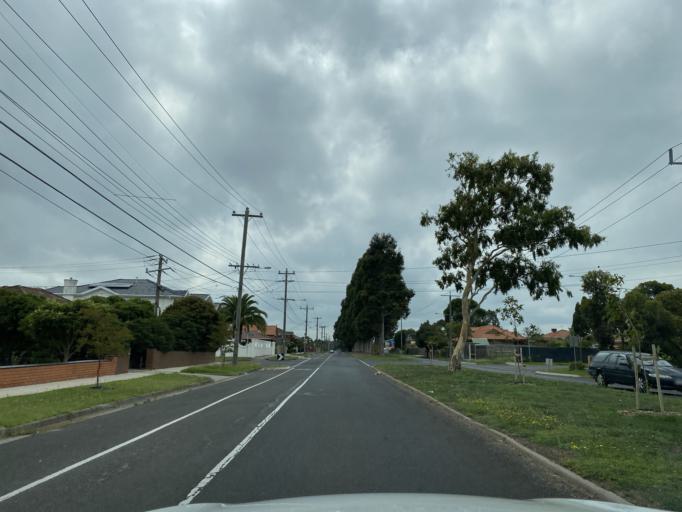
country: AU
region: Victoria
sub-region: Darebin
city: Reservoir
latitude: -37.6996
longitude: 145.0050
